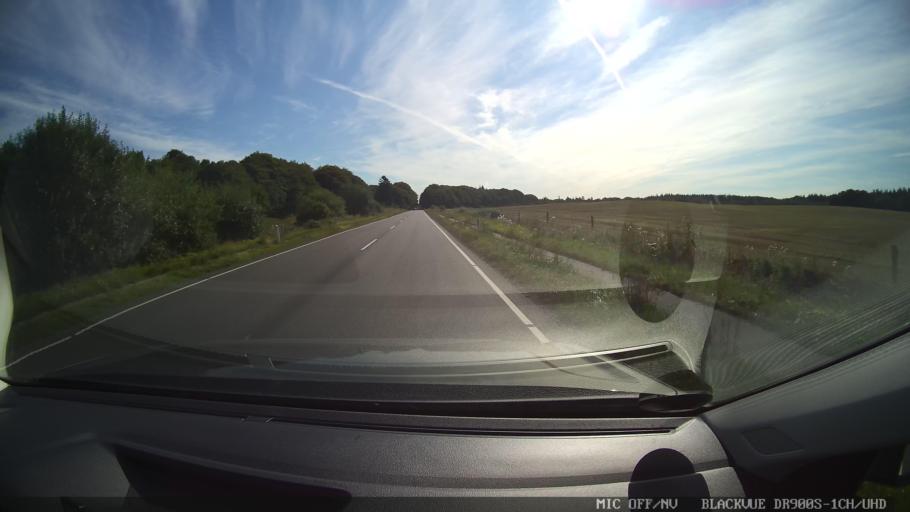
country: DK
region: North Denmark
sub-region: Mariagerfjord Kommune
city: Arden
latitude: 56.7832
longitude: 9.7359
